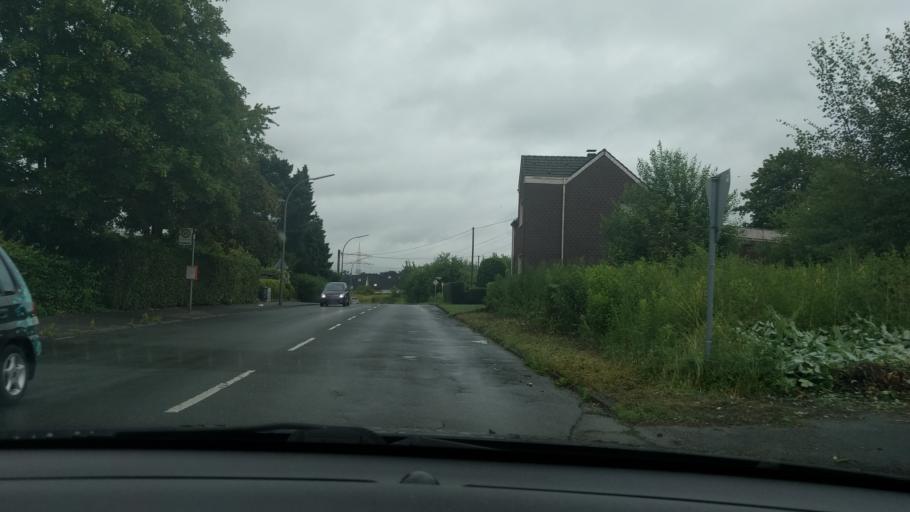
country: DE
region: North Rhine-Westphalia
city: Witten
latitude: 51.4808
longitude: 7.3856
